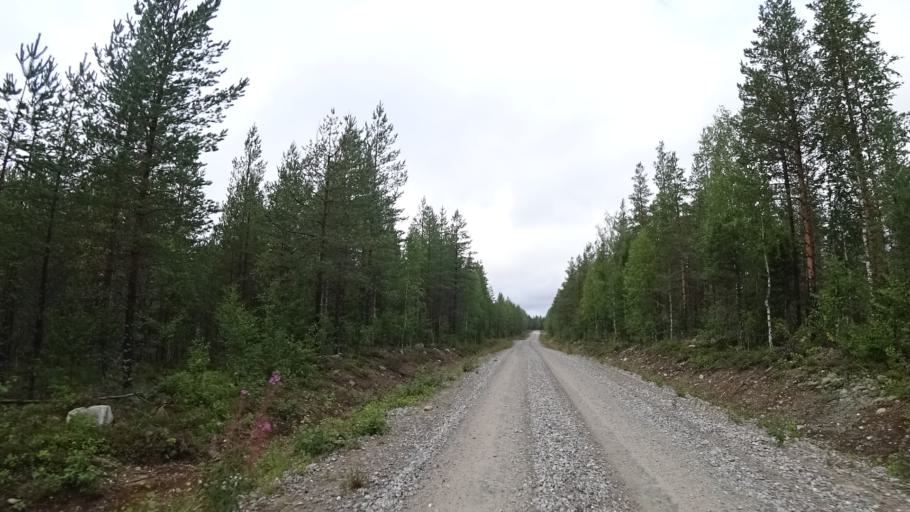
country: FI
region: North Karelia
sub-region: Pielisen Karjala
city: Lieksa
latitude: 63.4676
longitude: 30.2862
